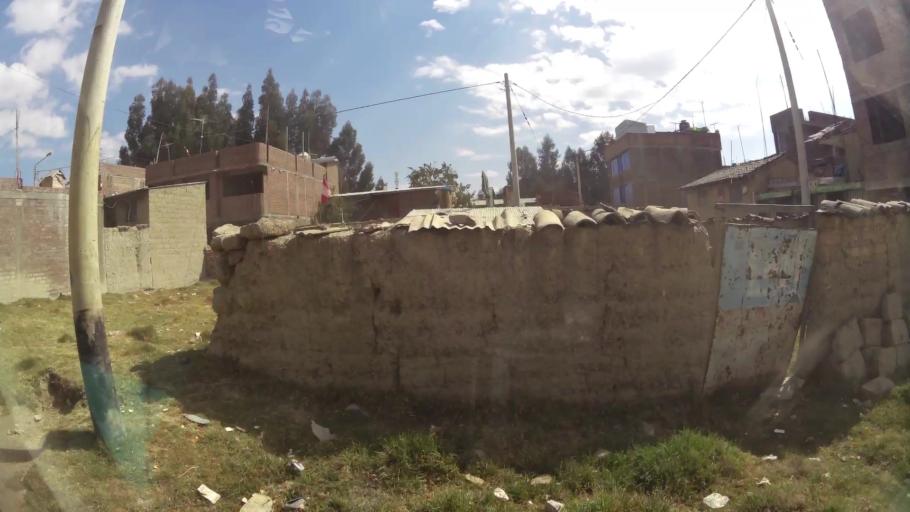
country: PE
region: Junin
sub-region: Provincia de Huancayo
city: Huancayo
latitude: -12.0952
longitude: -75.2038
